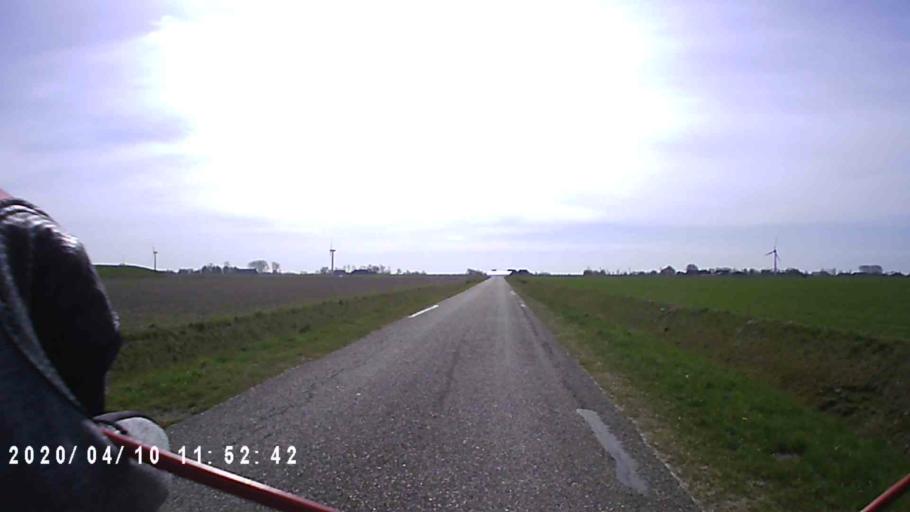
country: NL
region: Groningen
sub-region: Gemeente De Marne
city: Ulrum
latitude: 53.3933
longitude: 6.3313
